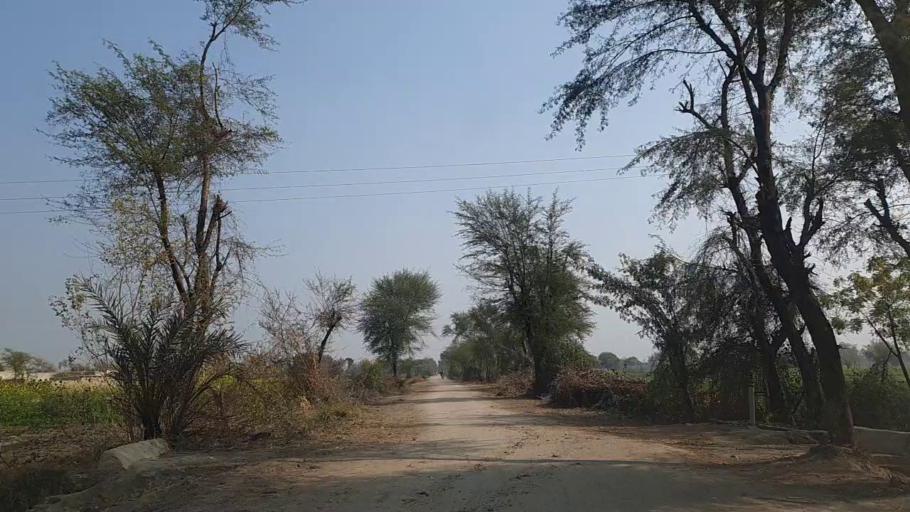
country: PK
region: Sindh
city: Daur
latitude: 26.3888
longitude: 68.4389
